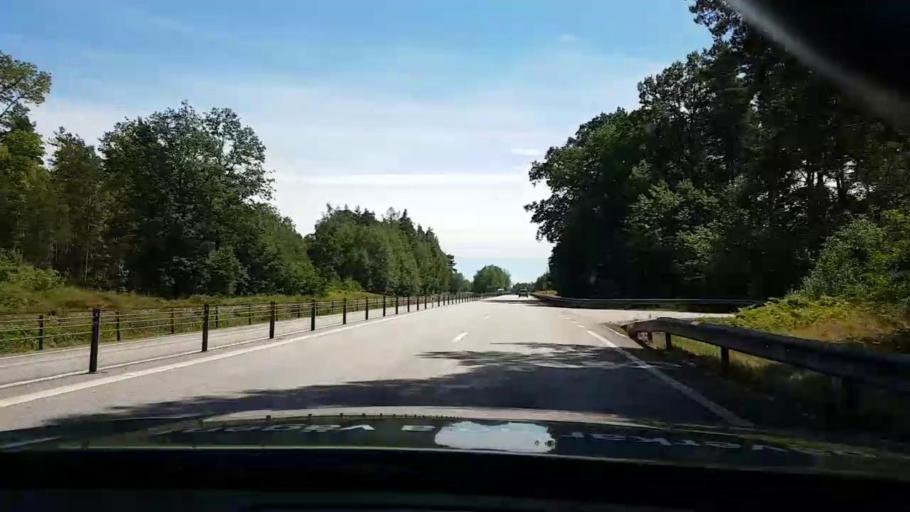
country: SE
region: Kalmar
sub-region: Vasterviks Kommun
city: Vaestervik
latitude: 57.7872
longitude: 16.5275
